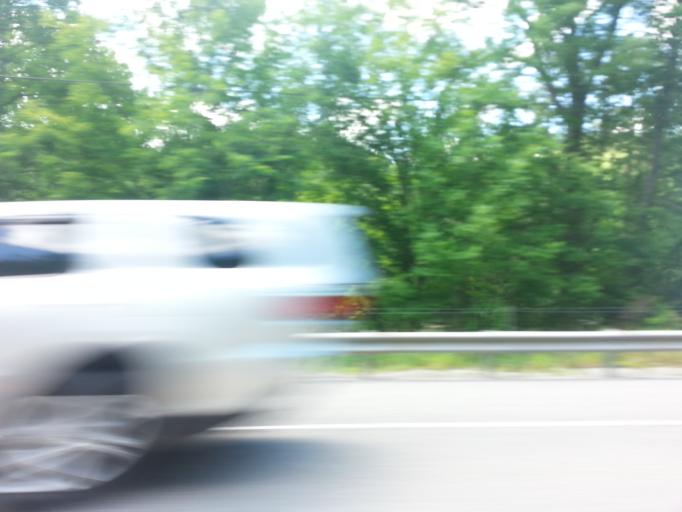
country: US
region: Kentucky
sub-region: Harlan County
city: Harlan
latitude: 36.8732
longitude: -83.3014
